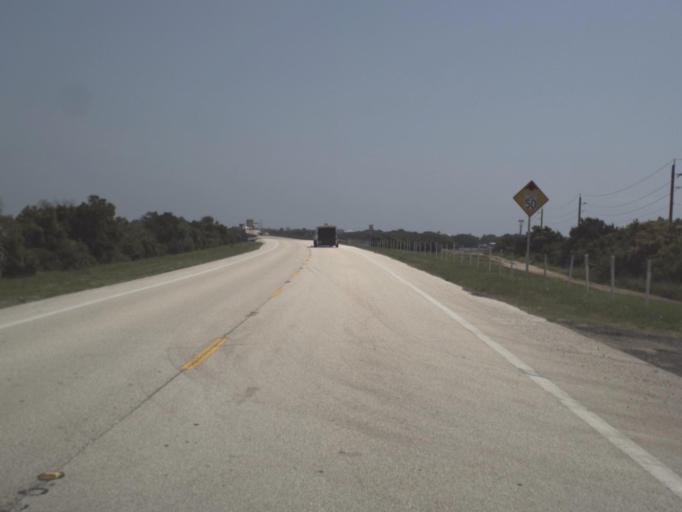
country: US
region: Florida
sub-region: Saint Johns County
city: Butler Beach
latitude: 29.7626
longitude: -81.2647
